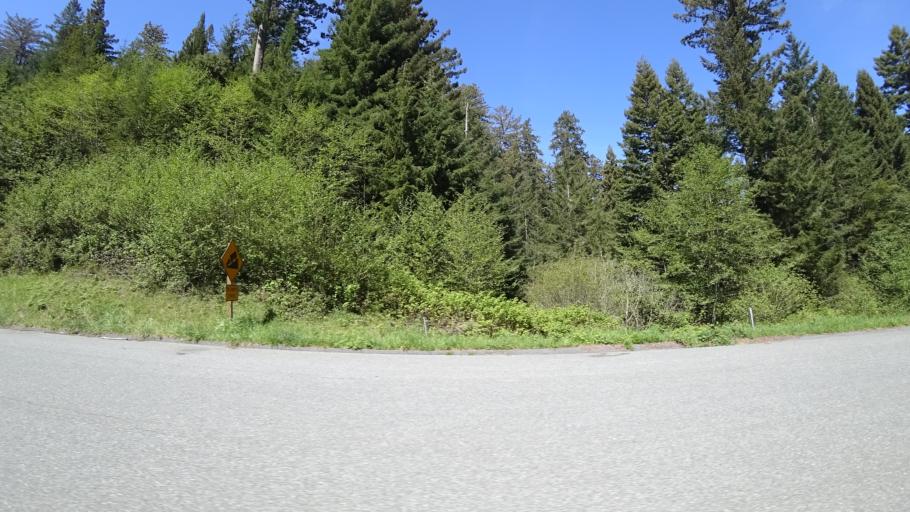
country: US
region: California
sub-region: Humboldt County
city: Westhaven-Moonstone
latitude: 41.3908
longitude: -123.9943
